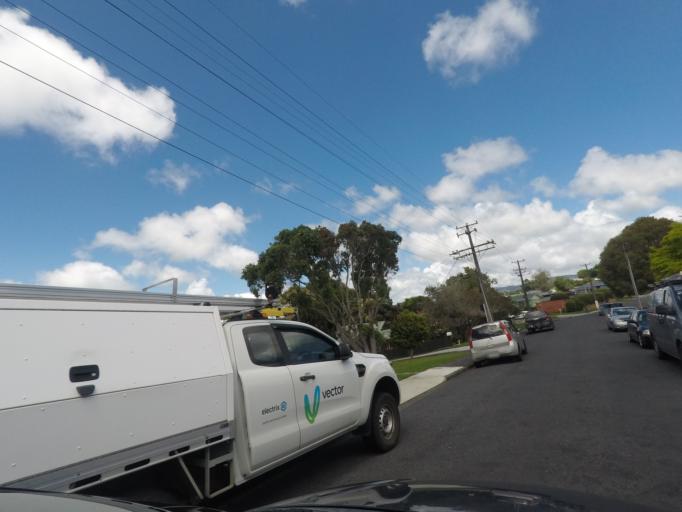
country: NZ
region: Auckland
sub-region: Auckland
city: Rosebank
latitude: -36.8713
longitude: 174.6492
